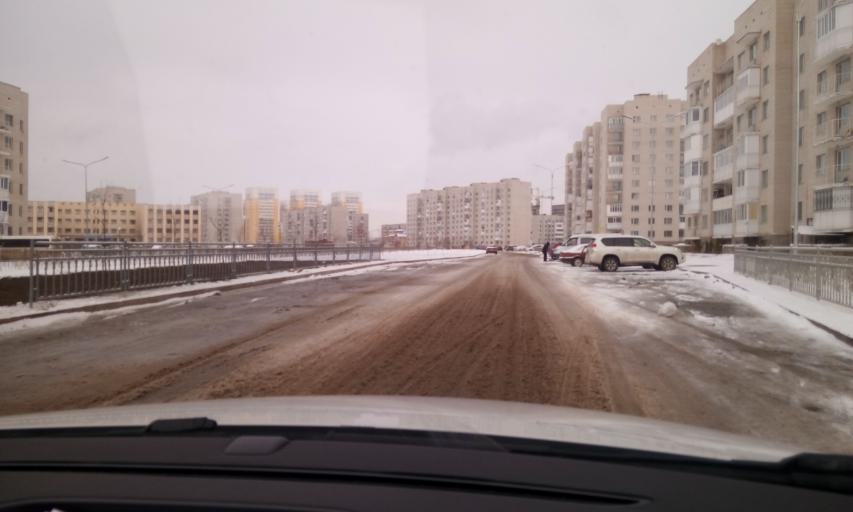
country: KZ
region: Astana Qalasy
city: Astana
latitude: 51.1225
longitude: 71.5045
